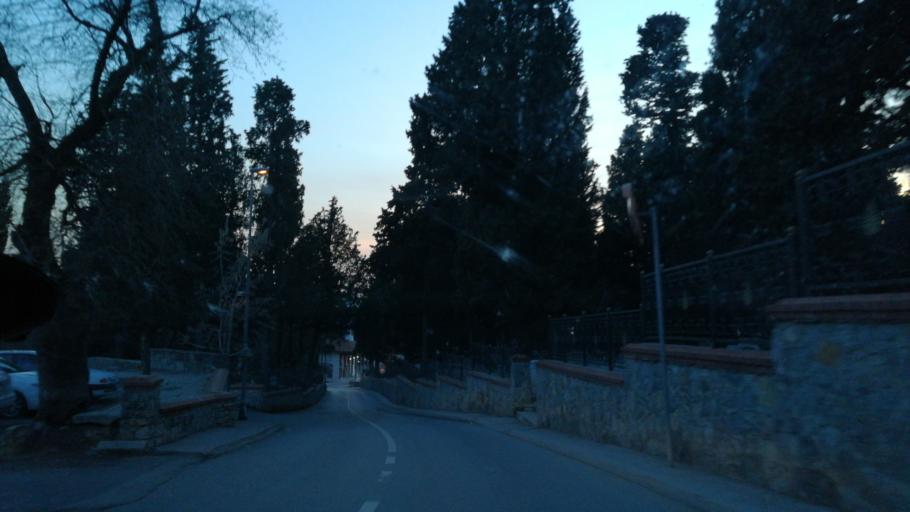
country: TR
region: Istanbul
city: UEskuedar
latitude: 41.0556
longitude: 29.0592
